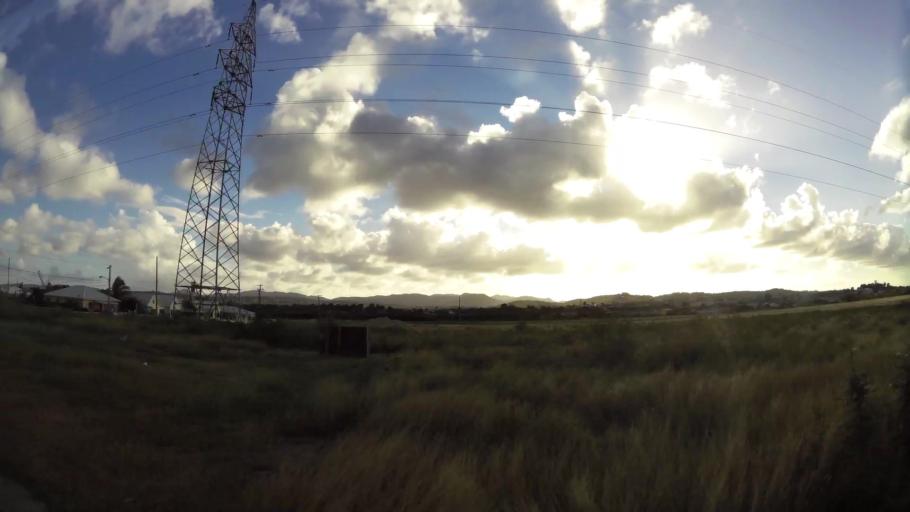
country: AG
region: Saint George
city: Piggotts
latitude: 17.1181
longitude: -61.7976
